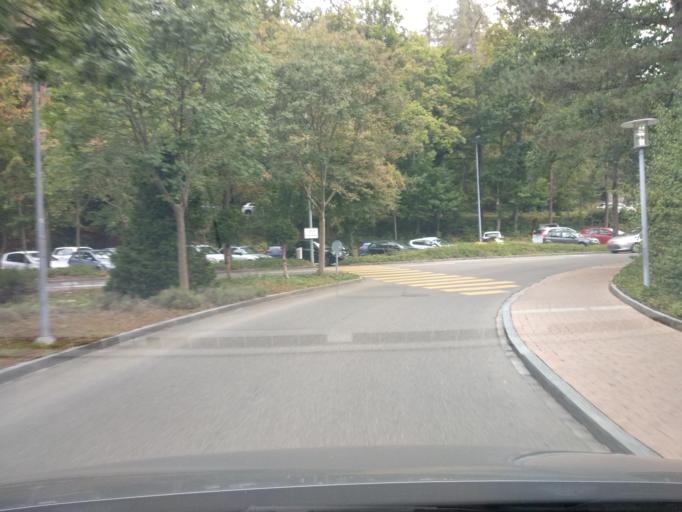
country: CH
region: Schaffhausen
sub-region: Bezirk Schaffhausen
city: Schaffhausen
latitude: 47.7126
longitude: 8.6354
